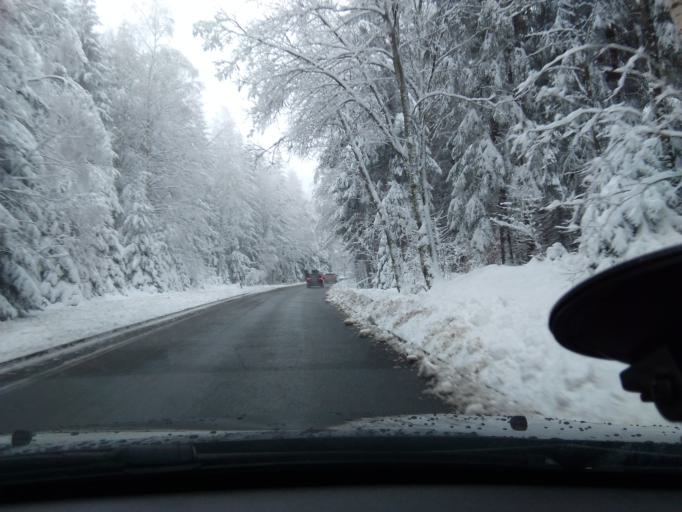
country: DE
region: Saxony
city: Markersbach
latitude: 50.5137
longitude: 12.8590
